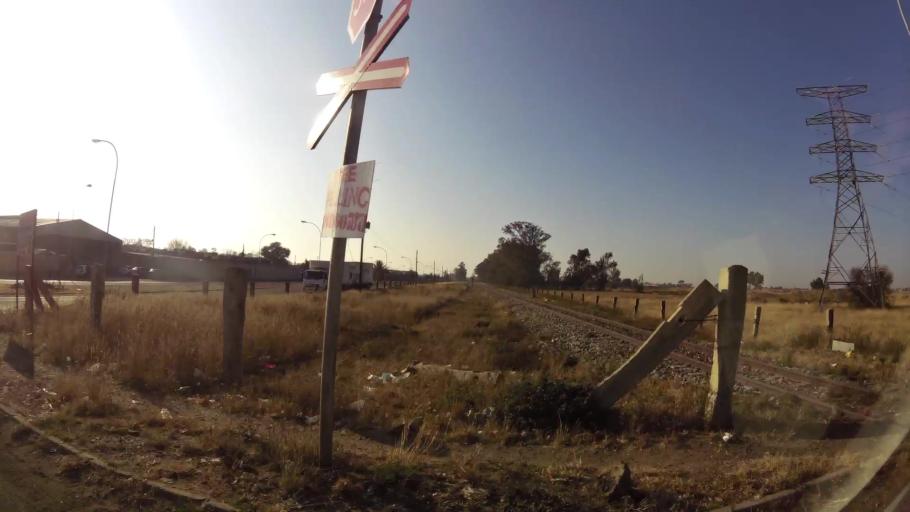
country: ZA
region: Orange Free State
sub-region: Mangaung Metropolitan Municipality
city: Bloemfontein
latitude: -29.1314
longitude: 26.2536
